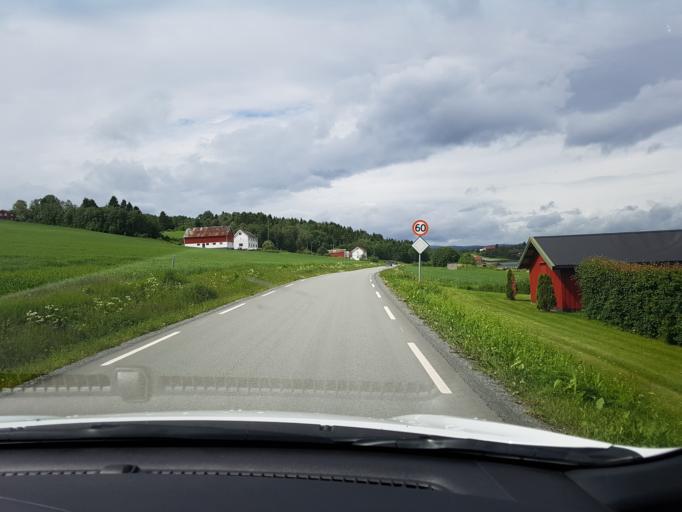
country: NO
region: Nord-Trondelag
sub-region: Frosta
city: Frosta
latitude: 63.6317
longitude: 10.8011
